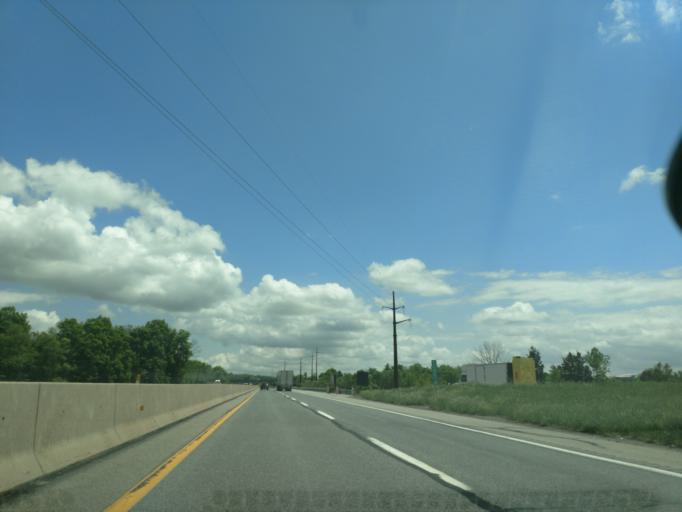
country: US
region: Pennsylvania
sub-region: Lancaster County
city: Swartzville
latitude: 40.2219
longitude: -76.0910
